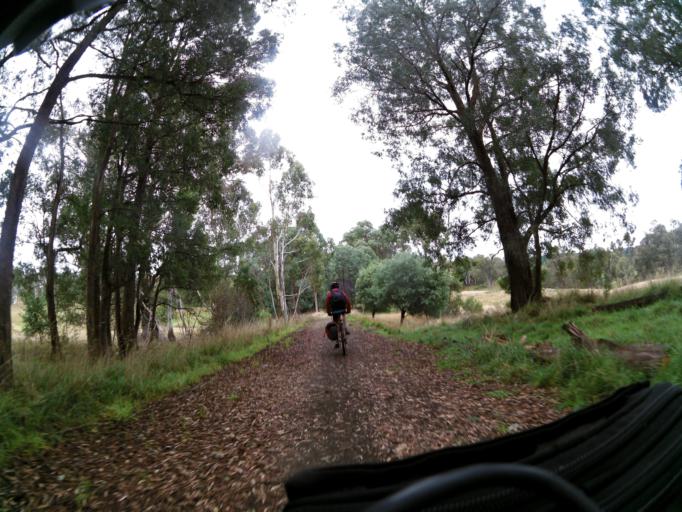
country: AU
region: New South Wales
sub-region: Greater Hume Shire
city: Holbrook
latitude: -36.1586
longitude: 147.4860
